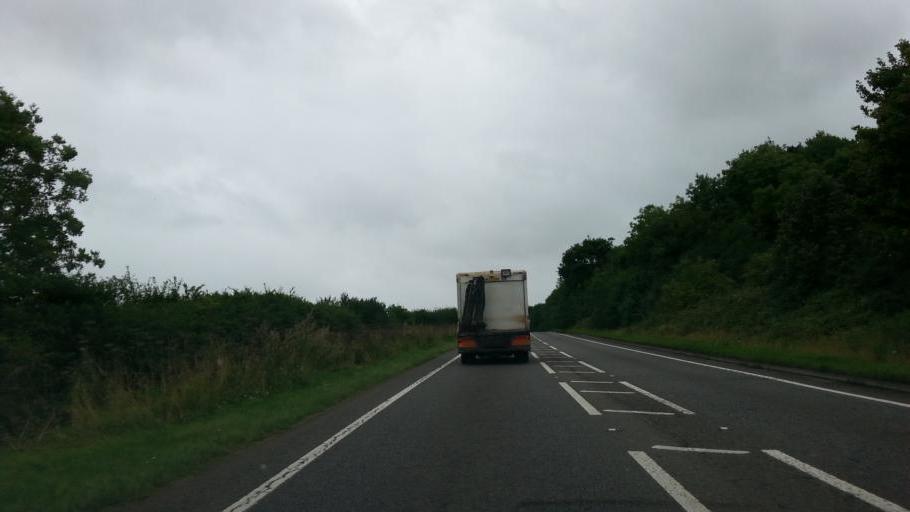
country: GB
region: England
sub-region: Northamptonshire
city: Oundle
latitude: 52.4475
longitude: -0.4655
